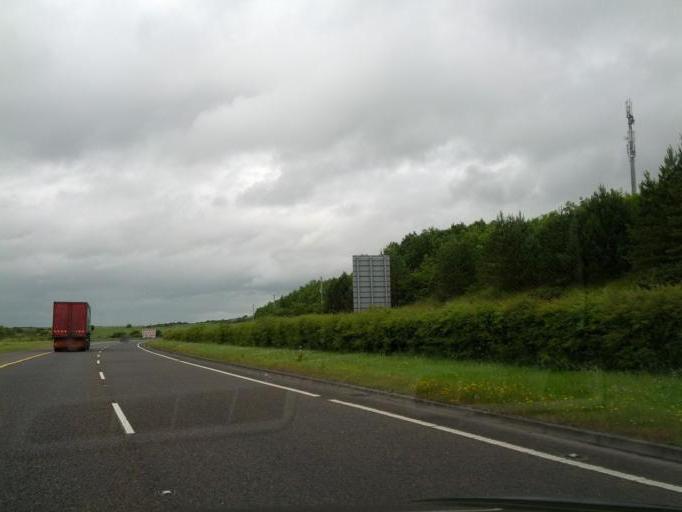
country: IE
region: Munster
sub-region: An Clar
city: Newmarket on Fergus
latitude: 52.7612
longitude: -8.9174
